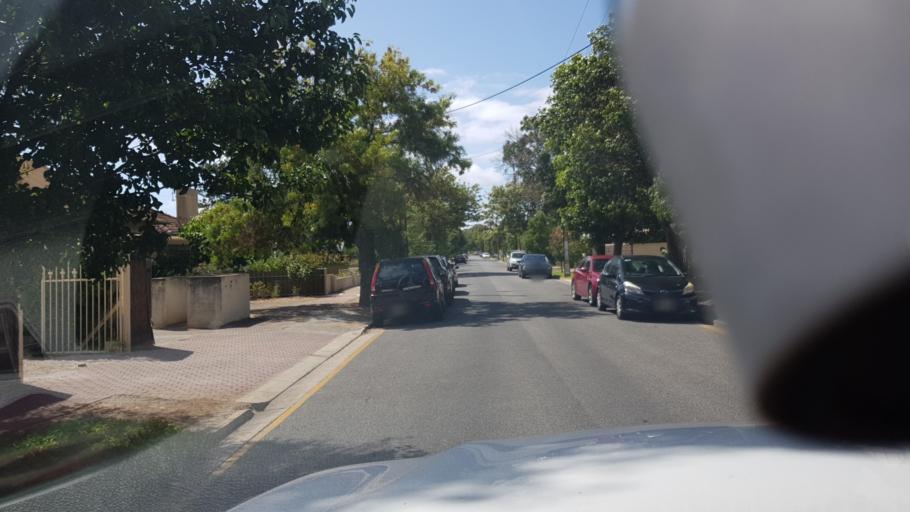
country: AU
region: South Australia
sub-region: Holdfast Bay
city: Glenelg East
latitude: -34.9786
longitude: 138.5314
